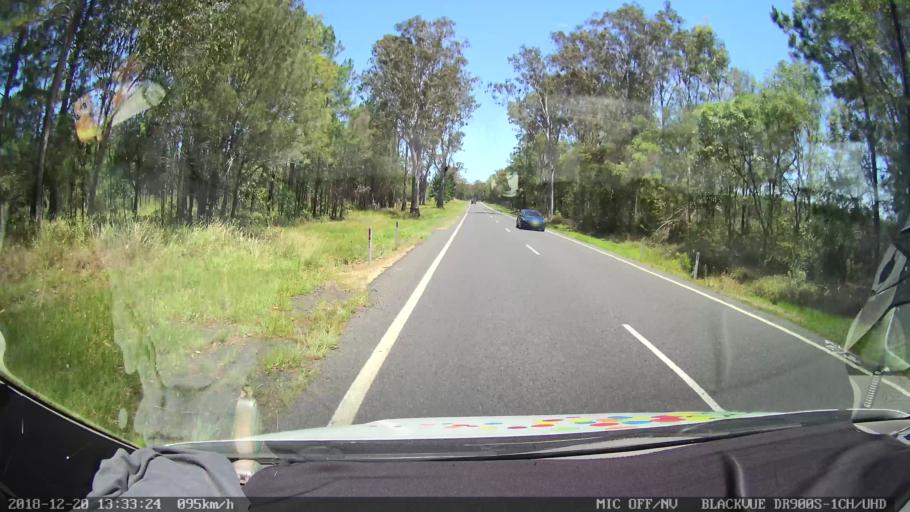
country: AU
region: New South Wales
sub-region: Clarence Valley
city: Gordon
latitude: -29.2450
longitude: 152.9866
